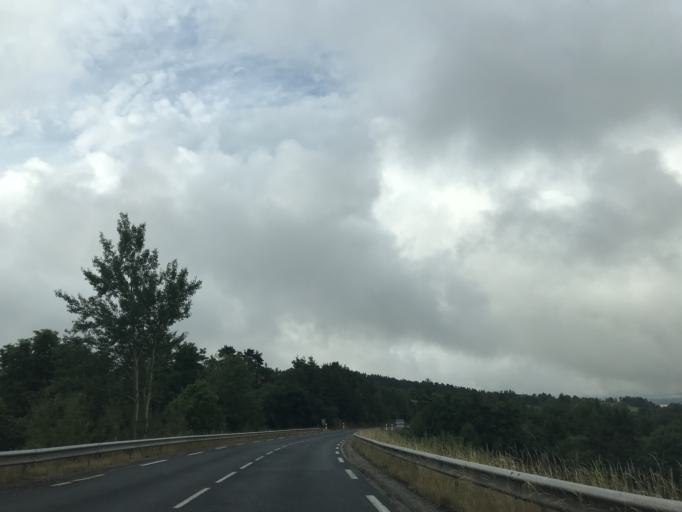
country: FR
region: Auvergne
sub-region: Departement de la Haute-Loire
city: Saint-Paulien
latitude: 45.1668
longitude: 3.8357
